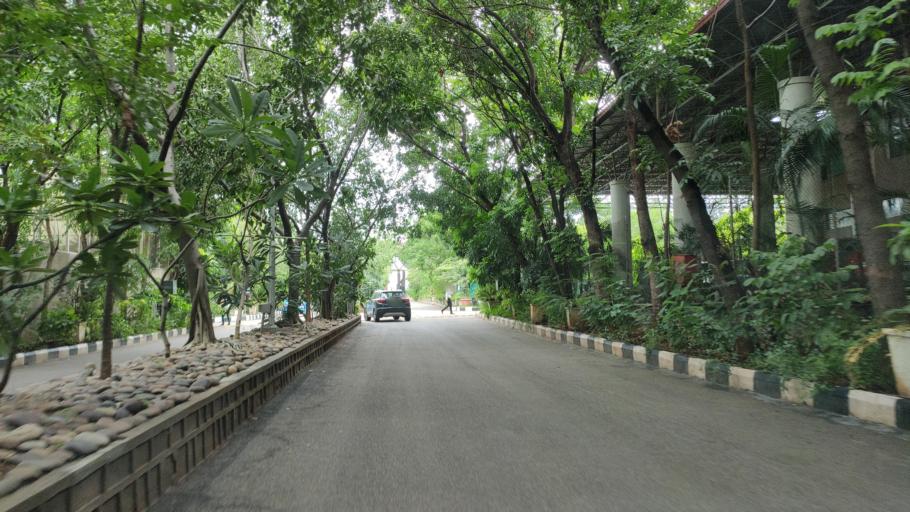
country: IN
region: Telangana
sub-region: Rangareddi
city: Secunderabad
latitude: 17.5794
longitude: 78.6013
